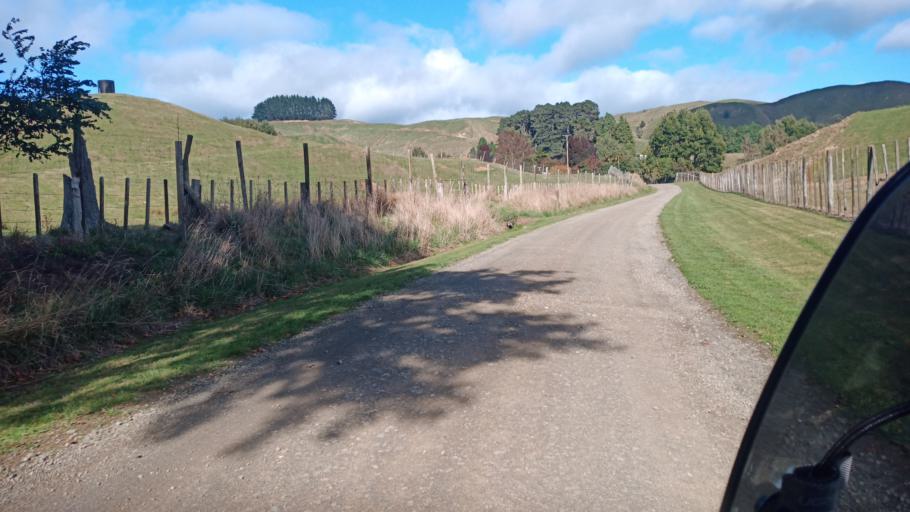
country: NZ
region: Bay of Plenty
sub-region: Opotiki District
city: Opotiki
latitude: -38.4605
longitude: 177.3858
